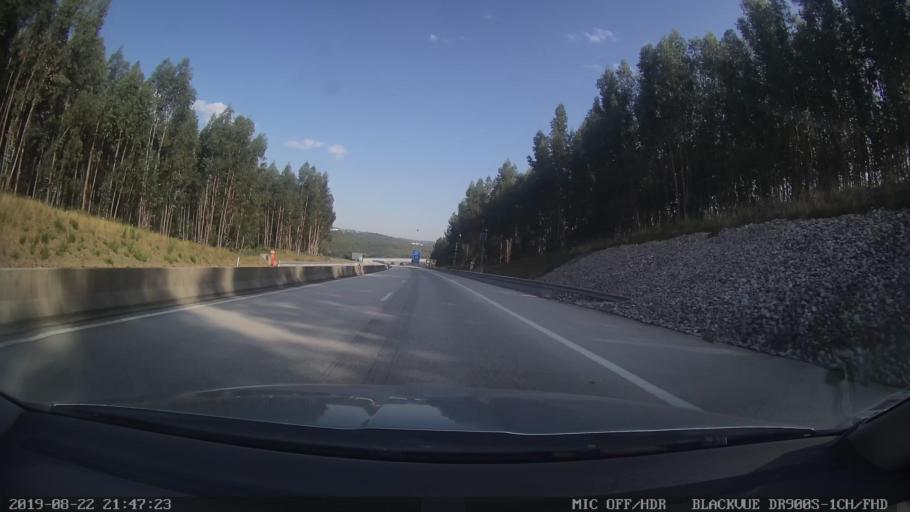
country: PT
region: Coimbra
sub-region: Penela
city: Penela
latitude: 40.0050
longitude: -8.3639
